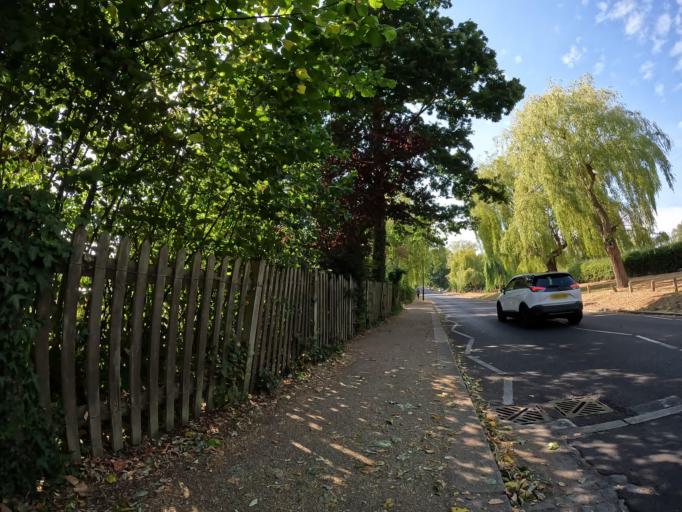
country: GB
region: England
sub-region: Hertfordshire
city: Potters Bar
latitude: 51.6897
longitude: -0.1579
